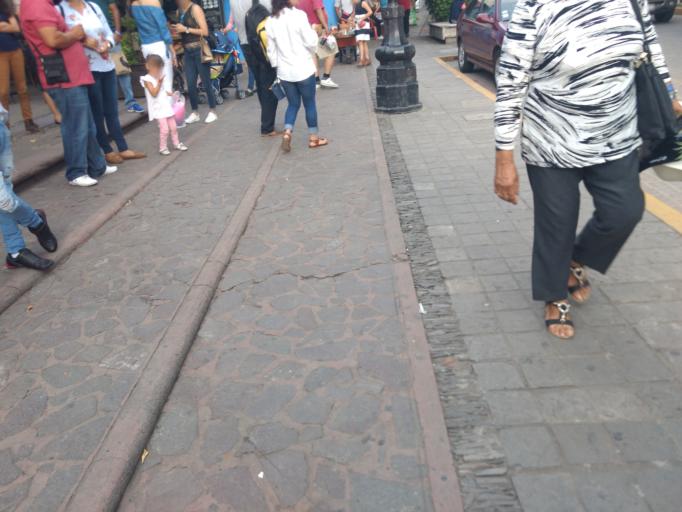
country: MX
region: Jalisco
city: Tequila
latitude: 20.8843
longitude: -103.8387
